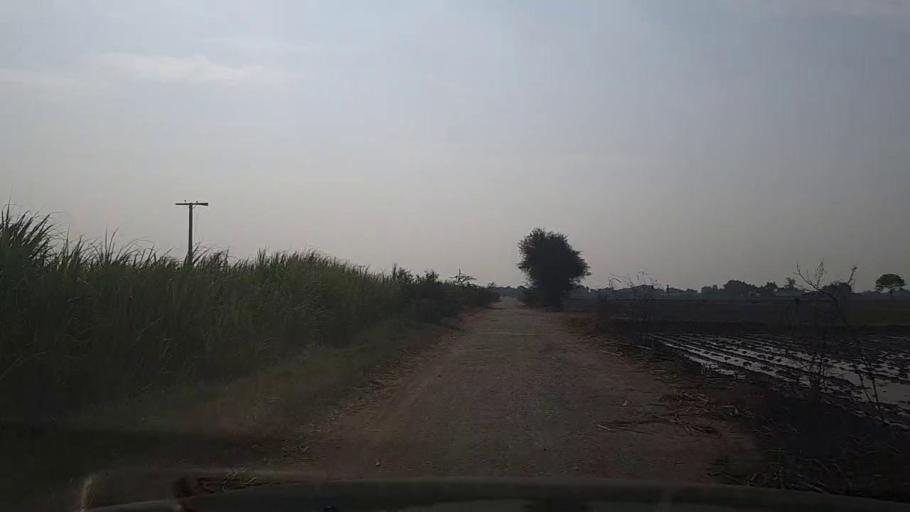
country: PK
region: Sindh
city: Bulri
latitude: 25.0127
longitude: 68.2998
